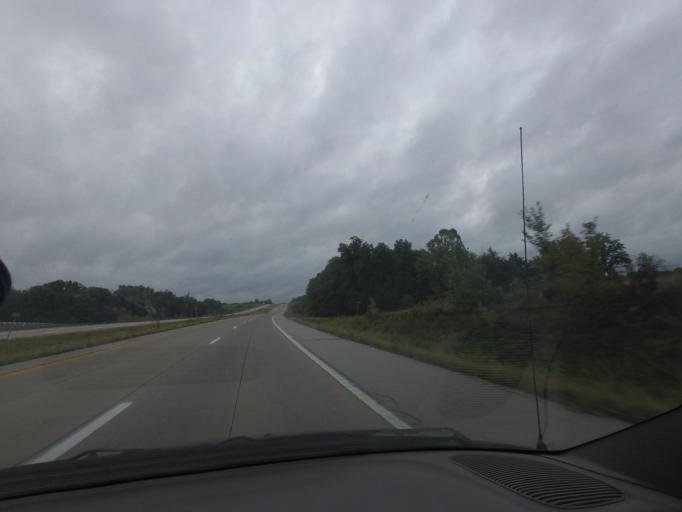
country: US
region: Missouri
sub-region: Shelby County
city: Shelbina
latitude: 39.6730
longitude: -91.8891
